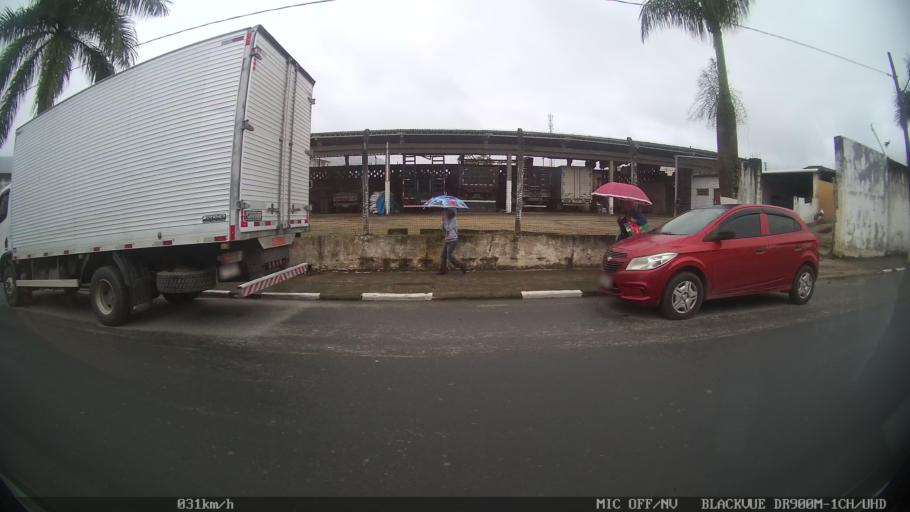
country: BR
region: Sao Paulo
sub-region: Juquia
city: Juquia
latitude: -24.3204
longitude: -47.6383
